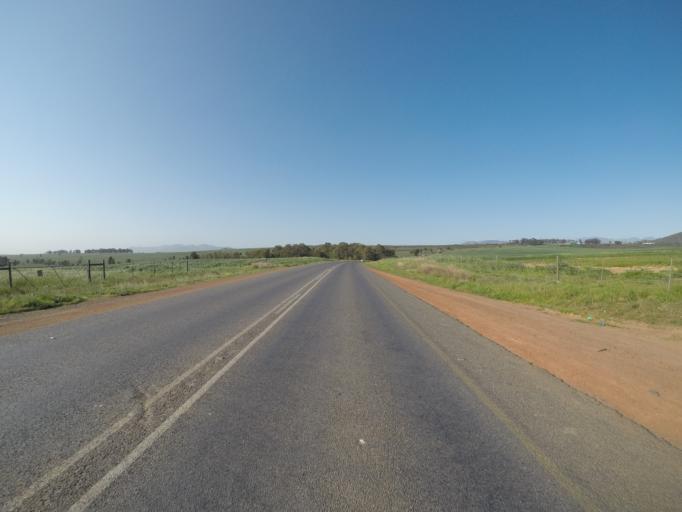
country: ZA
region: Western Cape
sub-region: City of Cape Town
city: Kraaifontein
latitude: -33.7670
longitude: 18.7590
